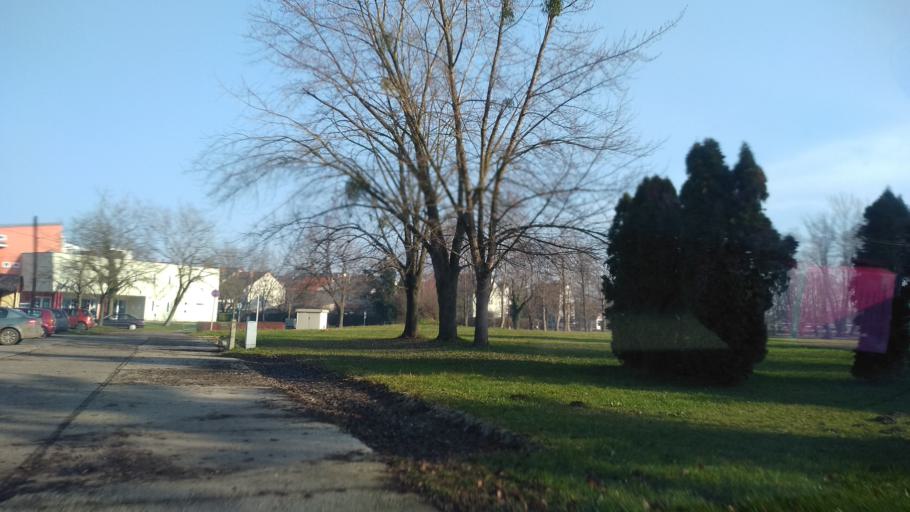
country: HU
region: Somogy
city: Barcs
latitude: 45.9559
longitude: 17.4607
